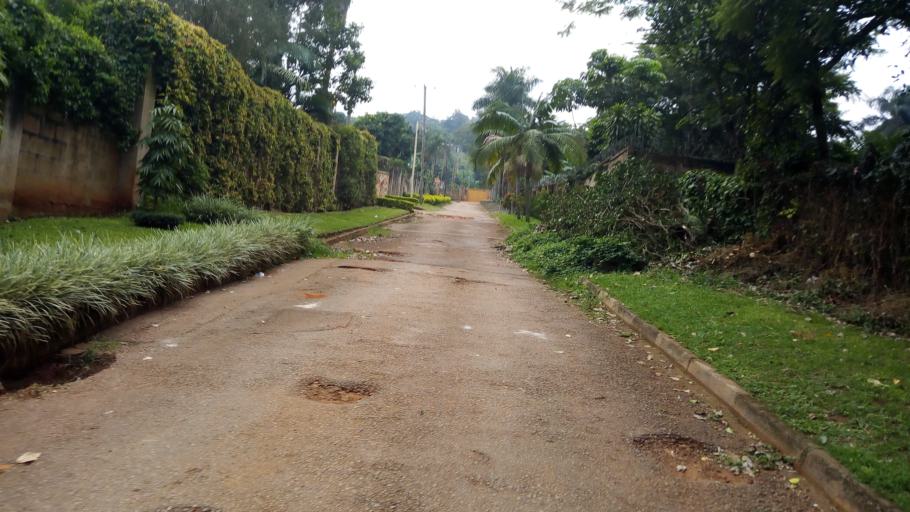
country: UG
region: Central Region
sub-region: Wakiso District
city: Kireka
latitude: 0.3201
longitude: 32.6292
